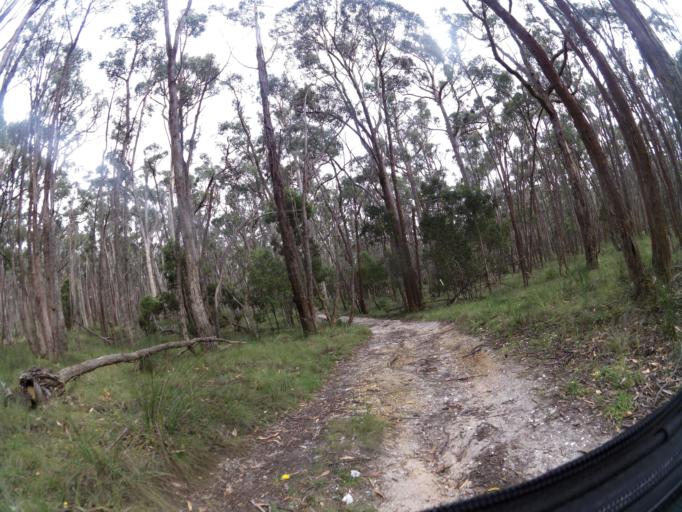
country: AU
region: Victoria
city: Brown Hill
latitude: -37.4738
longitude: 143.9121
